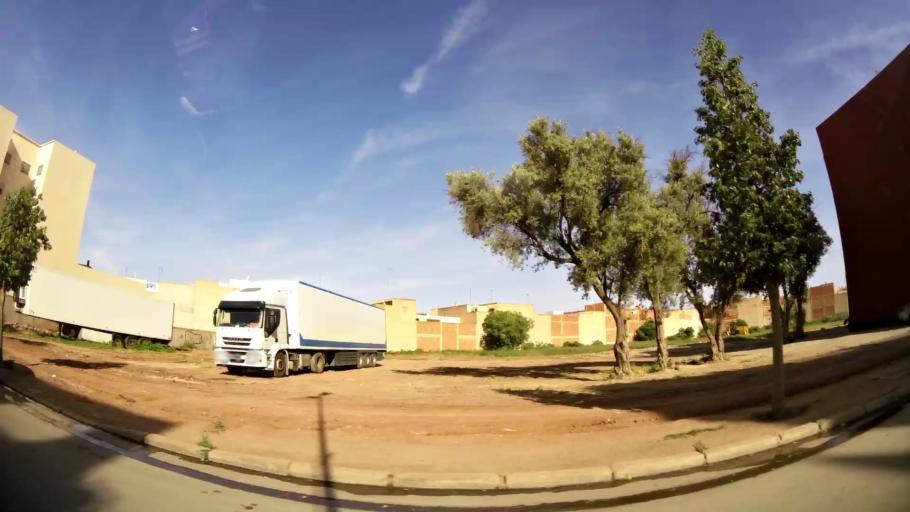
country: MA
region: Oriental
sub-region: Oujda-Angad
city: Oujda
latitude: 34.6683
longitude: -1.8953
